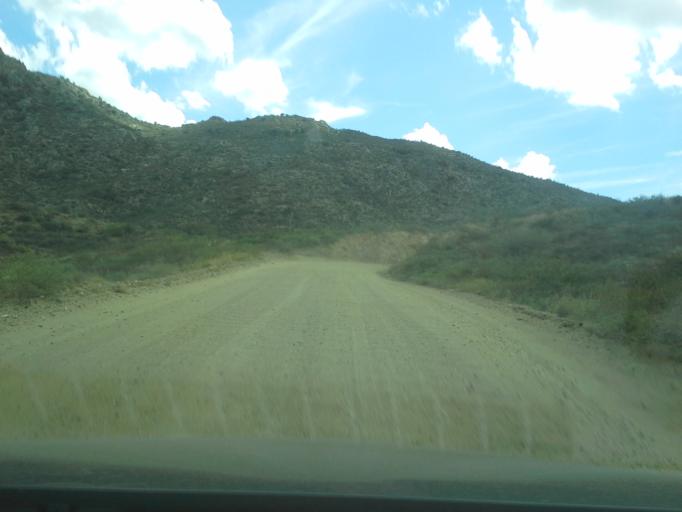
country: US
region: Arizona
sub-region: Yavapai County
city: Mayer
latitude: 34.2725
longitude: -112.2798
